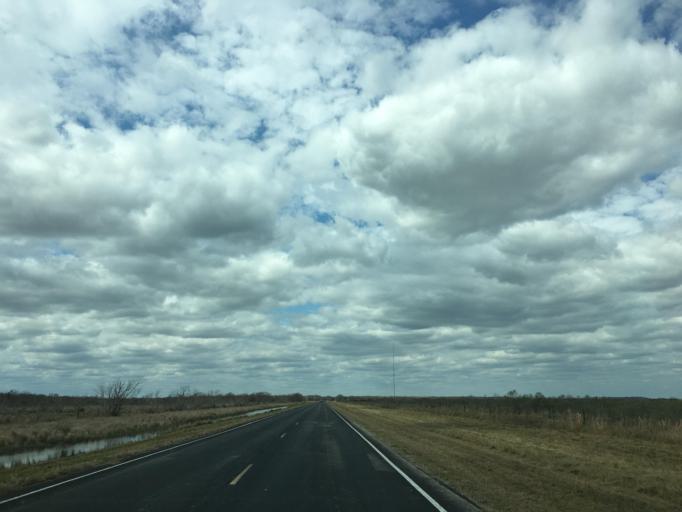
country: US
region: Texas
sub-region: Brazoria County
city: Oyster Creek
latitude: 29.0656
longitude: -95.3008
